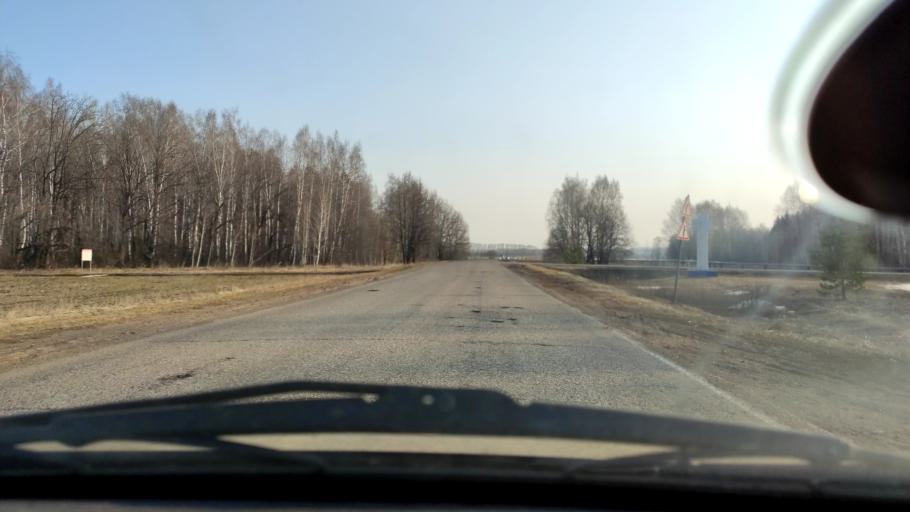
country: RU
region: Bashkortostan
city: Asanovo
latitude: 54.7996
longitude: 55.5327
